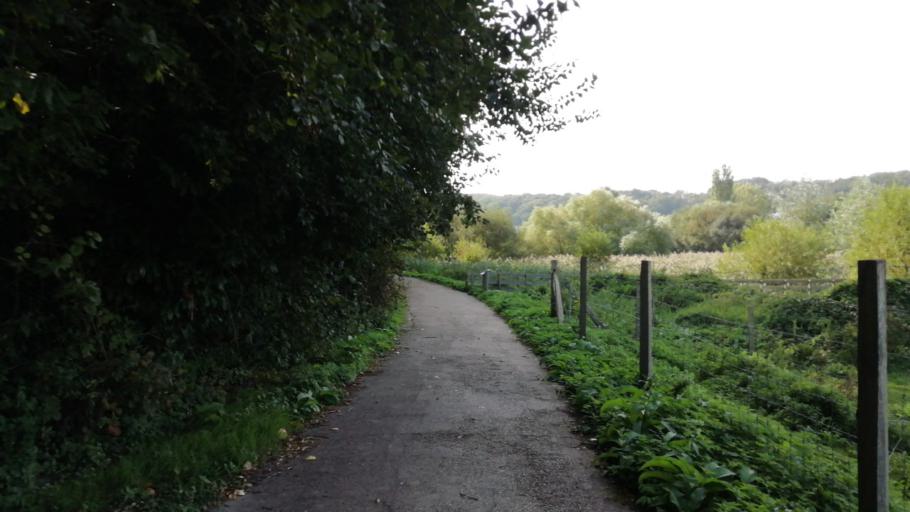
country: FR
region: Haute-Normandie
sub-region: Departement de la Seine-Maritime
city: Montivilliers
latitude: 49.5399
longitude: 0.1856
